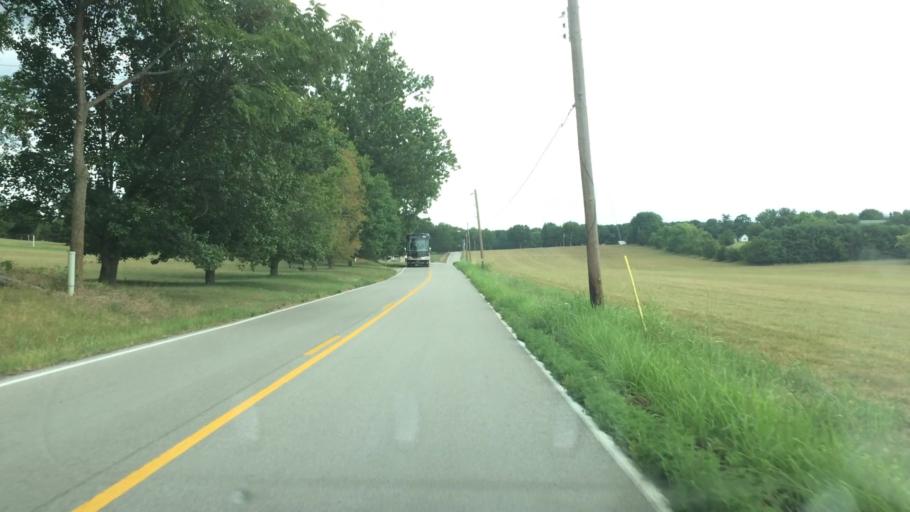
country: US
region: Missouri
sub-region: Greene County
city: Strafford
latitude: 37.1847
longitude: -93.1847
